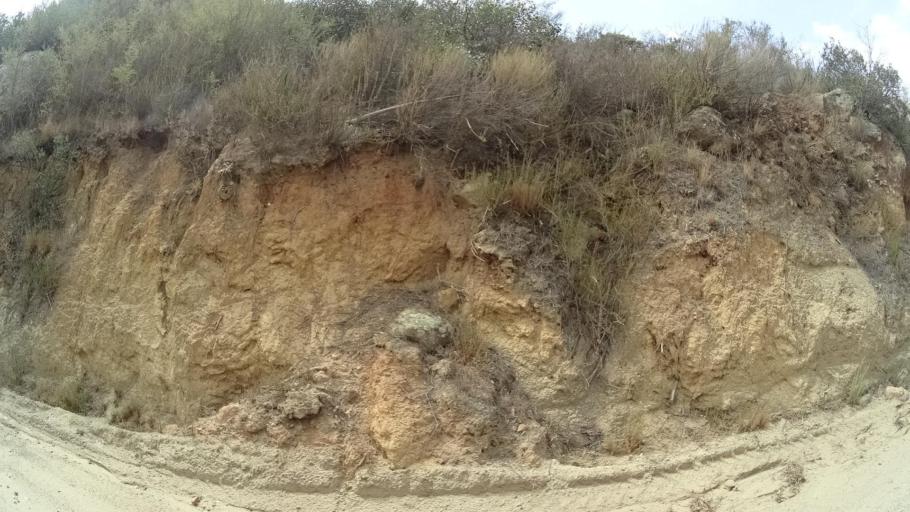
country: US
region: California
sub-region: San Diego County
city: Ramona
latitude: 33.1236
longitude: -116.8038
